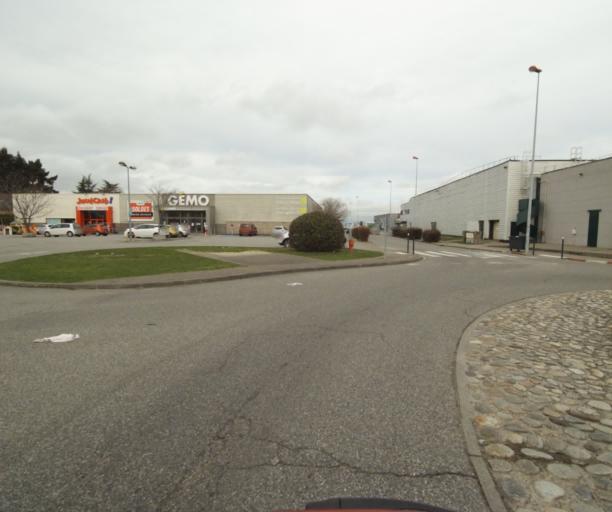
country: FR
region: Midi-Pyrenees
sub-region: Departement de l'Ariege
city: Saint-Jean-du-Falga
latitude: 43.1053
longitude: 1.6303
